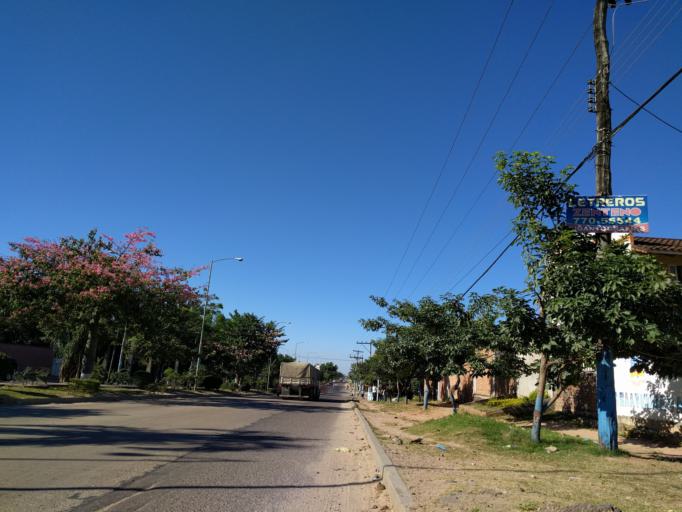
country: BO
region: Santa Cruz
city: Santa Cruz de la Sierra
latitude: -17.8472
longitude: -63.2481
